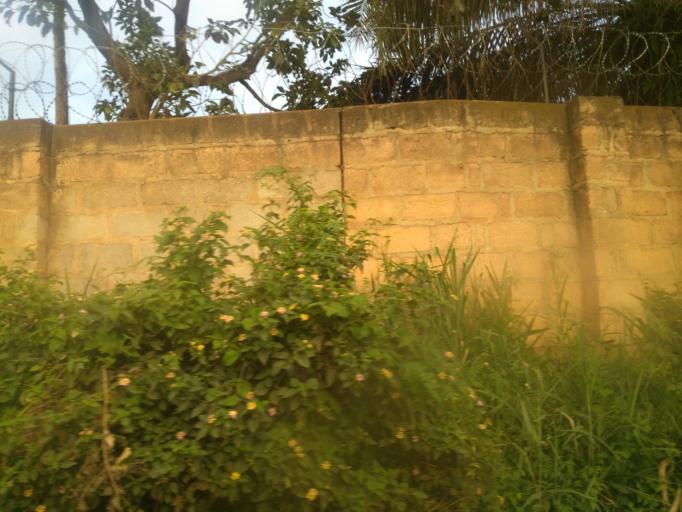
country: UG
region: Central Region
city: Kampala Central Division
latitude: 0.3472
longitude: 32.5950
